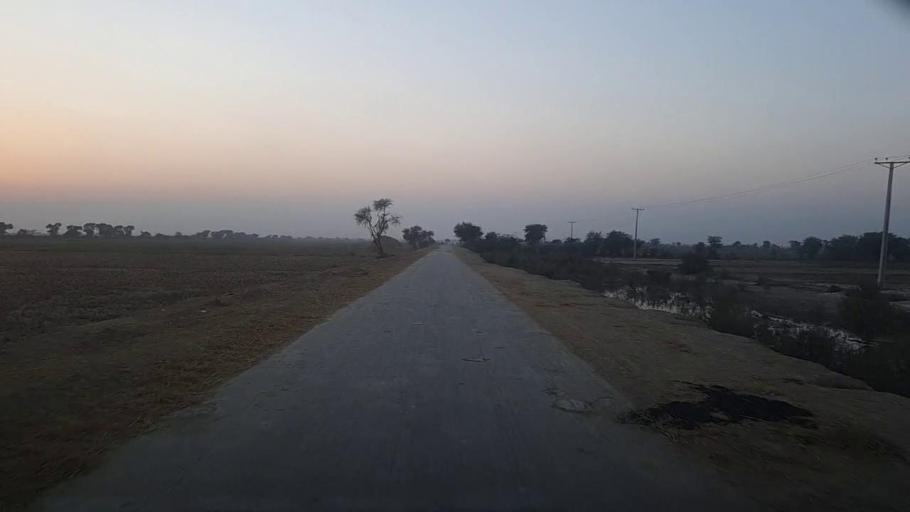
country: PK
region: Sindh
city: Khairpur Nathan Shah
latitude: 27.1782
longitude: 67.6257
